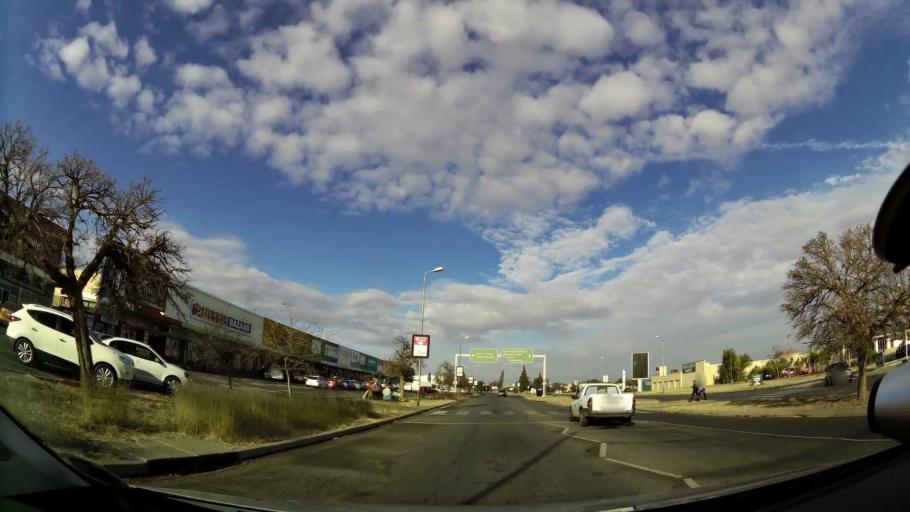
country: ZA
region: Orange Free State
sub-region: Lejweleputswa District Municipality
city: Welkom
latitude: -27.9853
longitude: 26.7332
